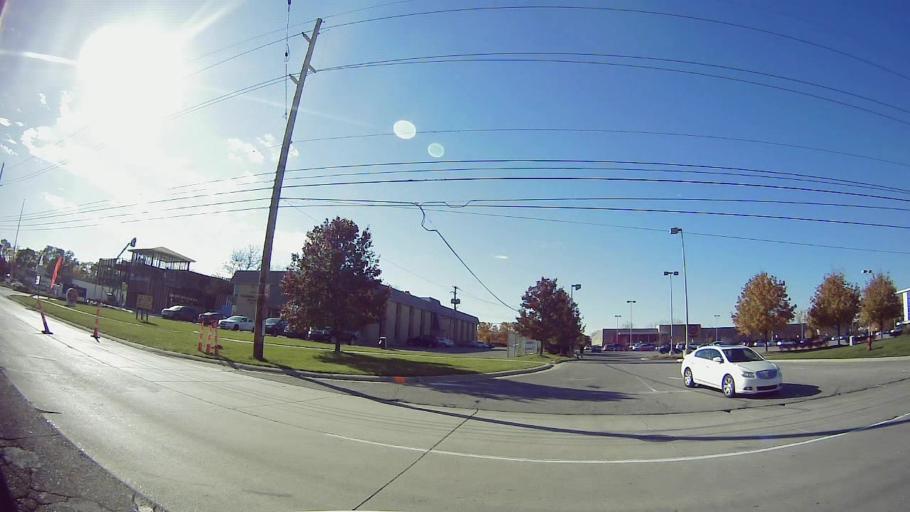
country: US
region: Michigan
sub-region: Oakland County
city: Beverly Hills
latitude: 42.5133
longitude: -83.2231
